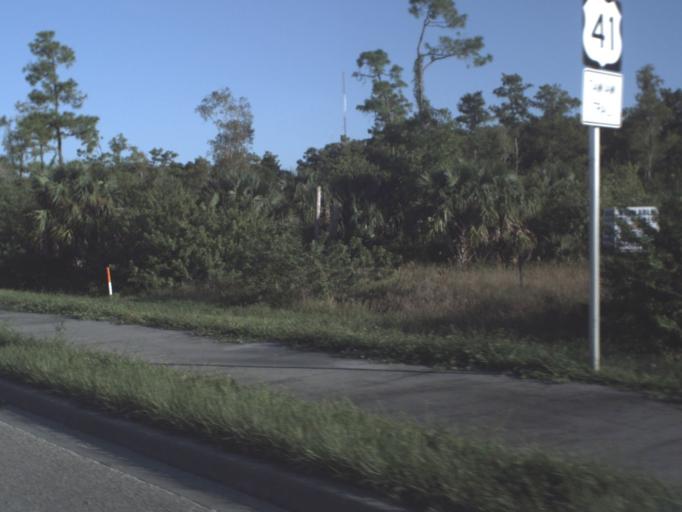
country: US
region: Florida
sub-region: Lee County
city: Villas
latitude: 26.4970
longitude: -81.8510
